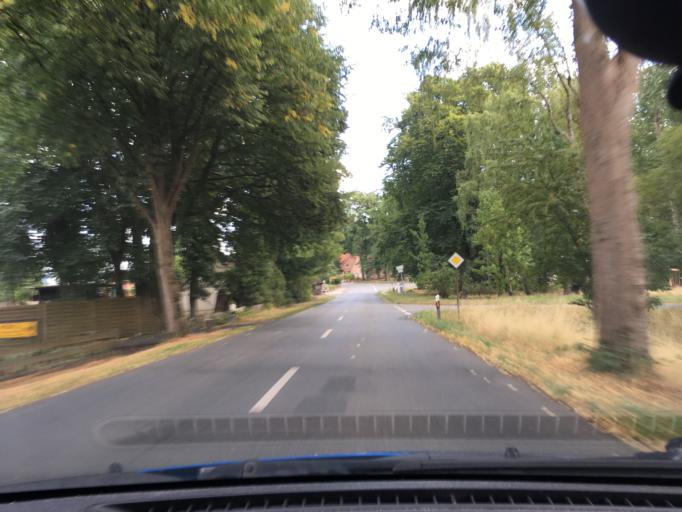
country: DE
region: Lower Saxony
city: Wriedel
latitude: 53.0324
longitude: 10.2813
